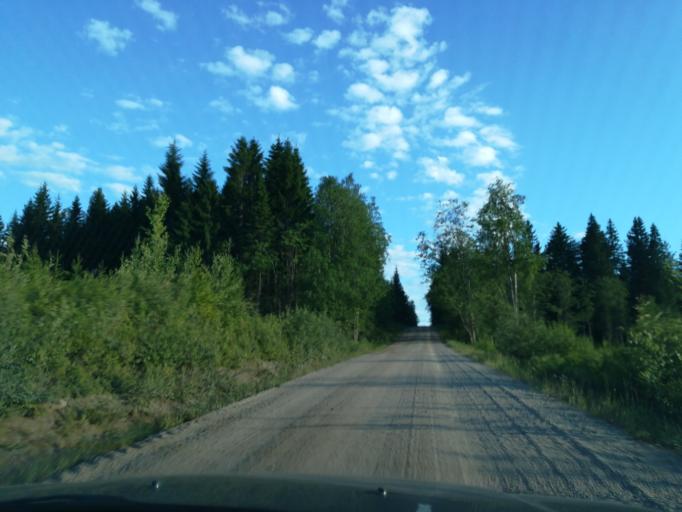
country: FI
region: Southern Savonia
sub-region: Mikkeli
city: Puumala
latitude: 61.5948
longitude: 28.1157
